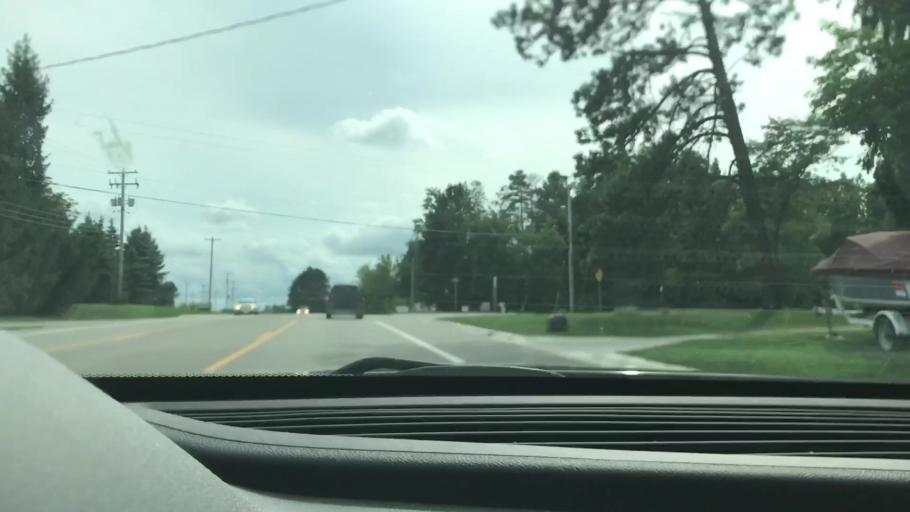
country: US
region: Michigan
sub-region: Missaukee County
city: Lake City
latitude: 44.3159
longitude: -85.2139
